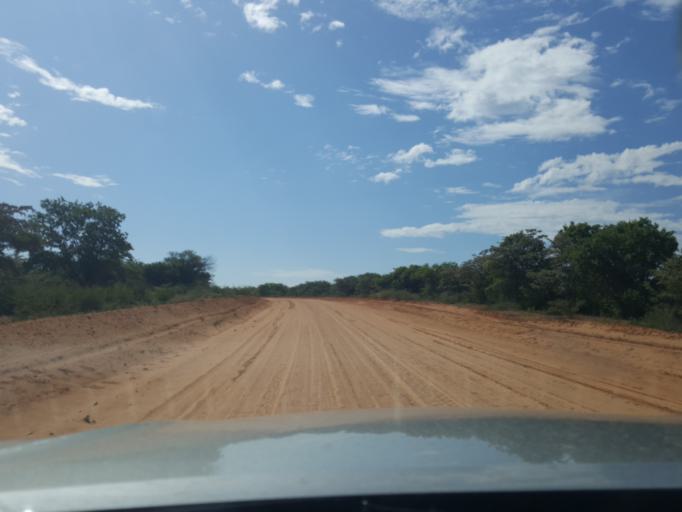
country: BW
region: Kweneng
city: Khudumelapye
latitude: -23.8080
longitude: 24.8168
